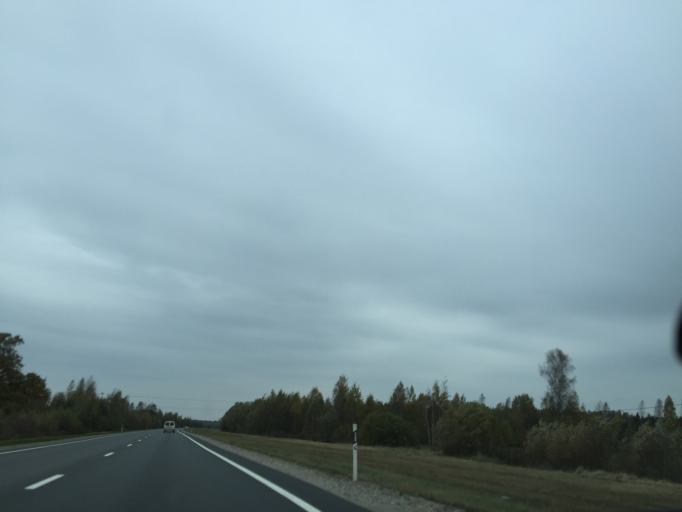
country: LV
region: Ozolnieku
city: Ozolnieki
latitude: 56.6789
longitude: 23.8224
